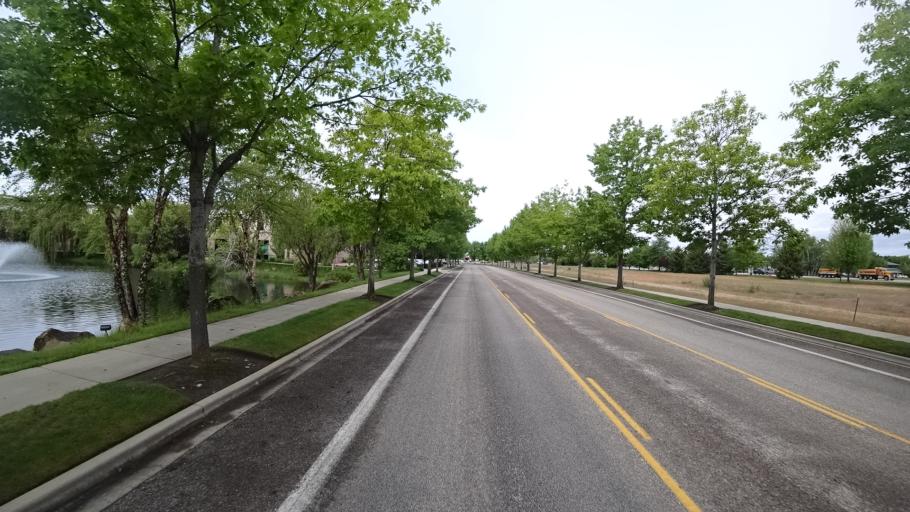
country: US
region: Idaho
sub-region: Ada County
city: Eagle
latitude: 43.6895
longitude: -116.3492
